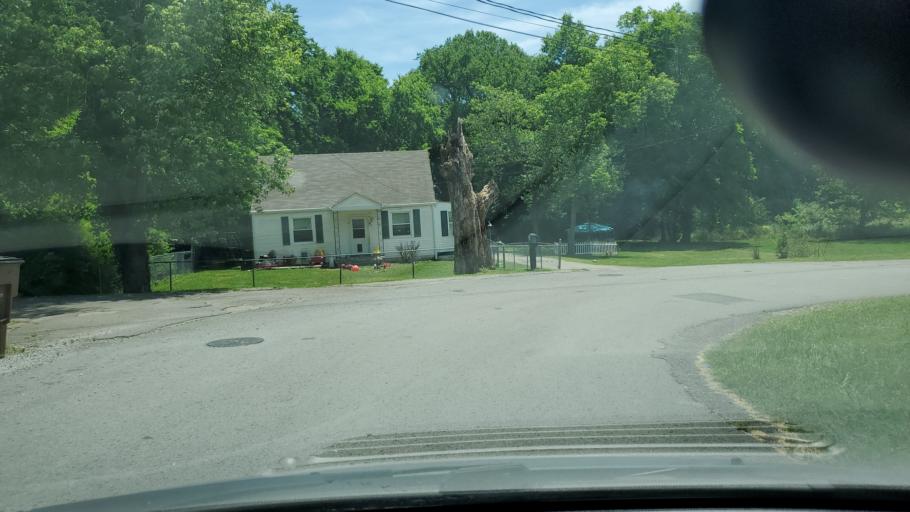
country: US
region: Tennessee
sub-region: Davidson County
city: Nashville
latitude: 36.2177
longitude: -86.7590
